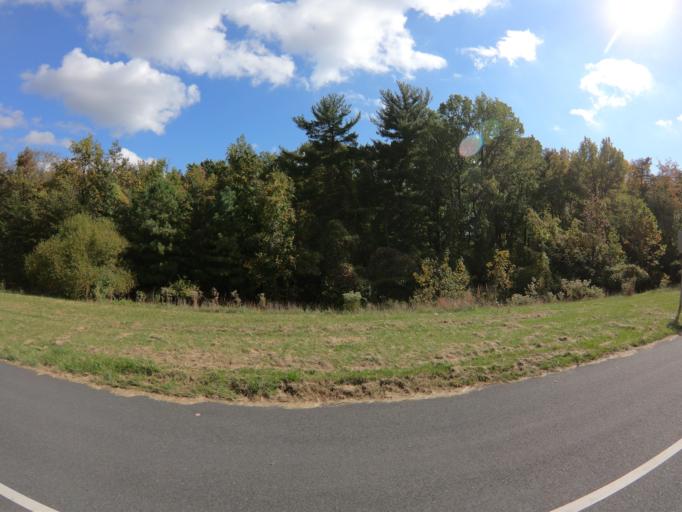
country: US
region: Maryland
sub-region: Anne Arundel County
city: Jessup
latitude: 39.1574
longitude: -76.7433
